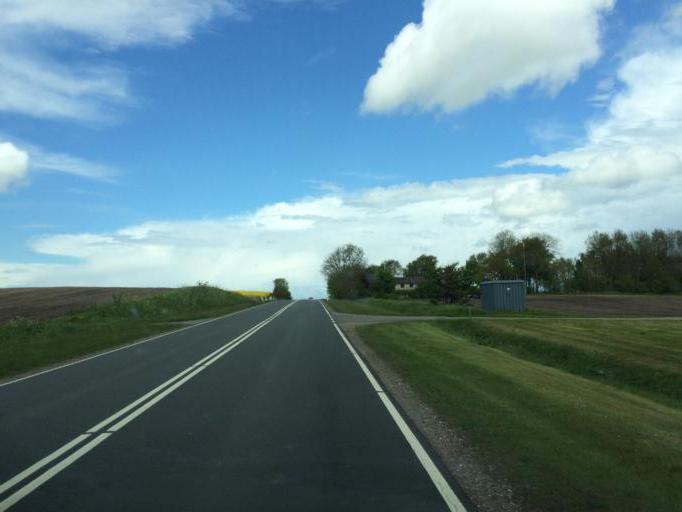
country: DK
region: North Denmark
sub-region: Vesthimmerland Kommune
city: Farso
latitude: 56.7955
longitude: 9.3524
